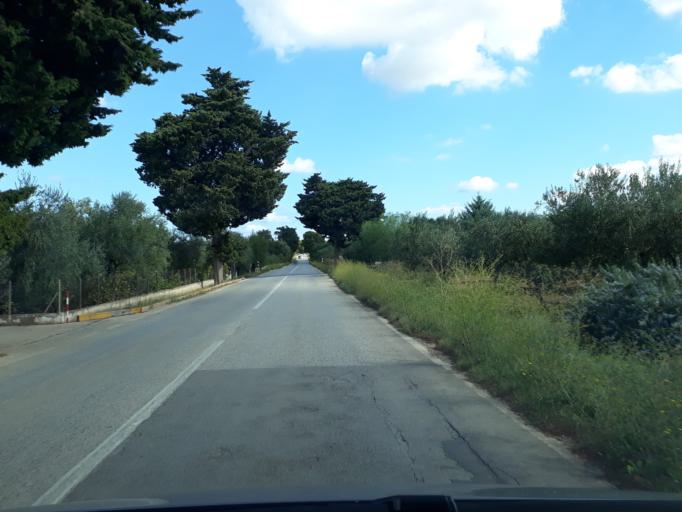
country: IT
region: Apulia
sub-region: Provincia di Bari
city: Rutigliano
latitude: 41.0205
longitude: 17.0250
